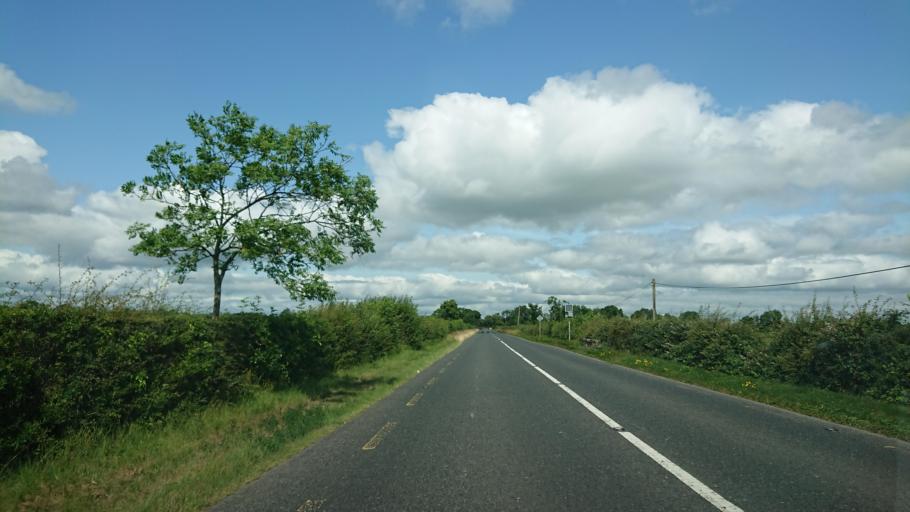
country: IE
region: Leinster
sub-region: Kildare
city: Kilcock
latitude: 53.3656
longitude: -6.6988
